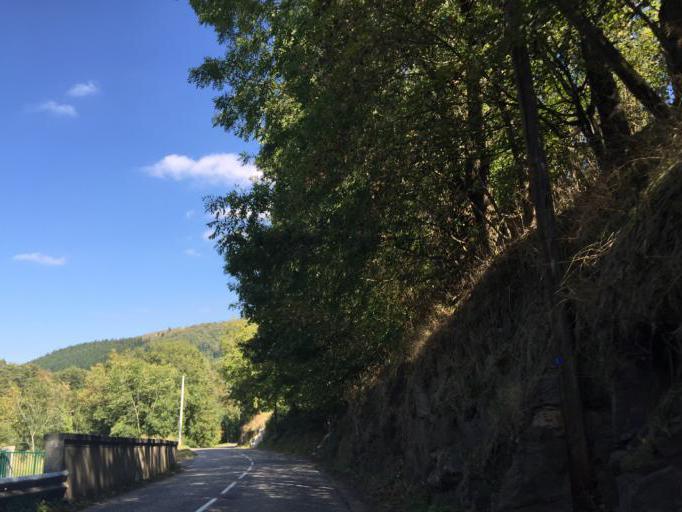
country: FR
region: Rhone-Alpes
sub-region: Departement de la Loire
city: Saint-Paul-en-Jarez
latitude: 45.4447
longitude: 4.5803
